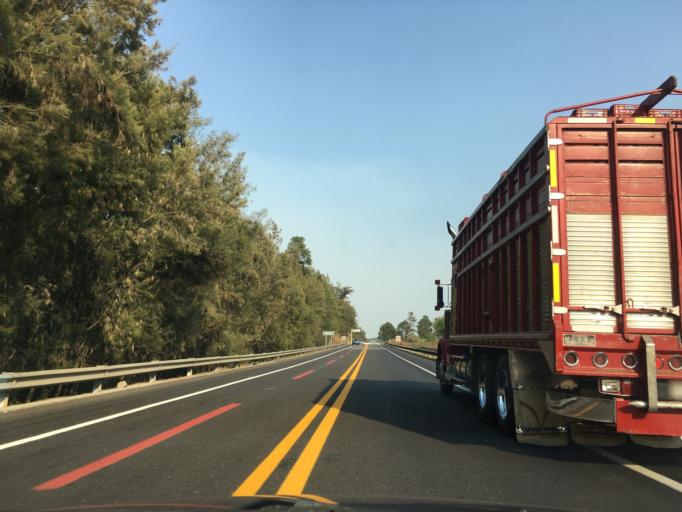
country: MX
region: Michoacan
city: Tingambato
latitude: 19.4373
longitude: -101.8269
